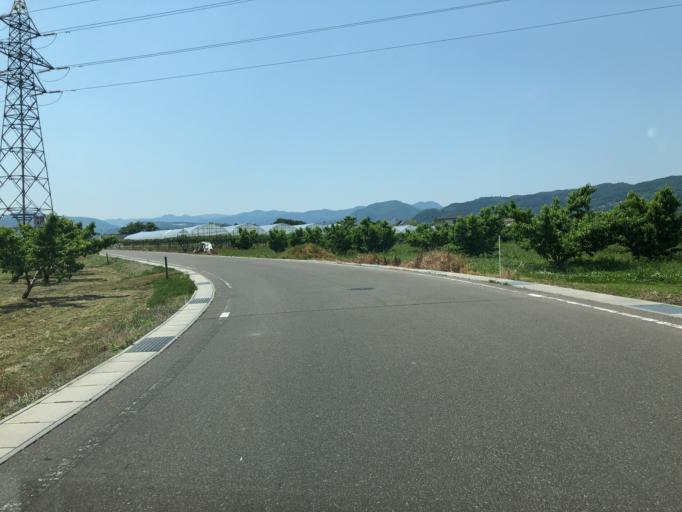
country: JP
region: Fukushima
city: Hobaramachi
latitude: 37.8193
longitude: 140.4842
